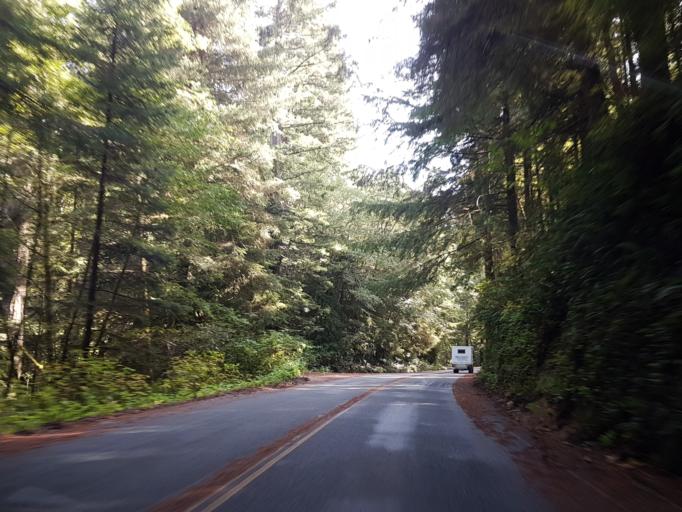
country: US
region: California
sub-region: Del Norte County
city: Bertsch-Oceanview
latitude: 41.4543
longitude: -124.0434
